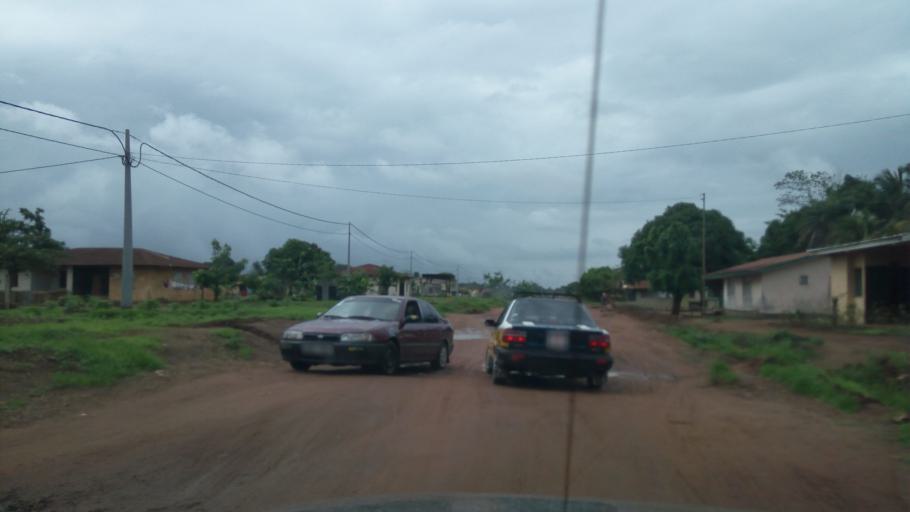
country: SL
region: Northern Province
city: Tintafor
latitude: 8.6257
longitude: -13.2156
